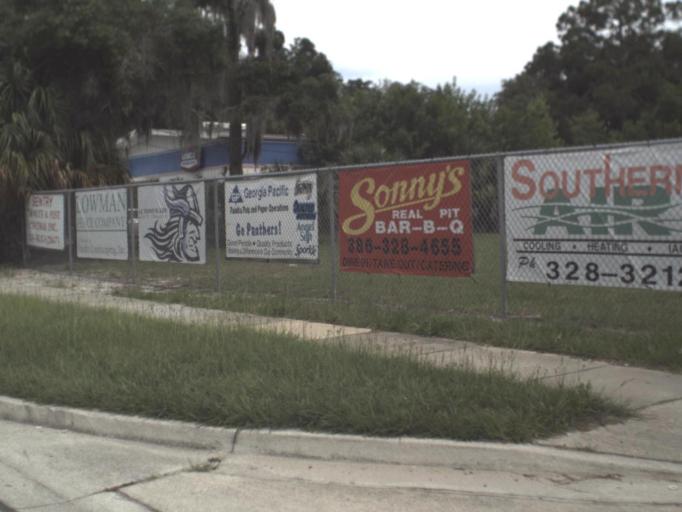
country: US
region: Florida
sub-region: Putnam County
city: Palatka
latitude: 29.6416
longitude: -81.6690
